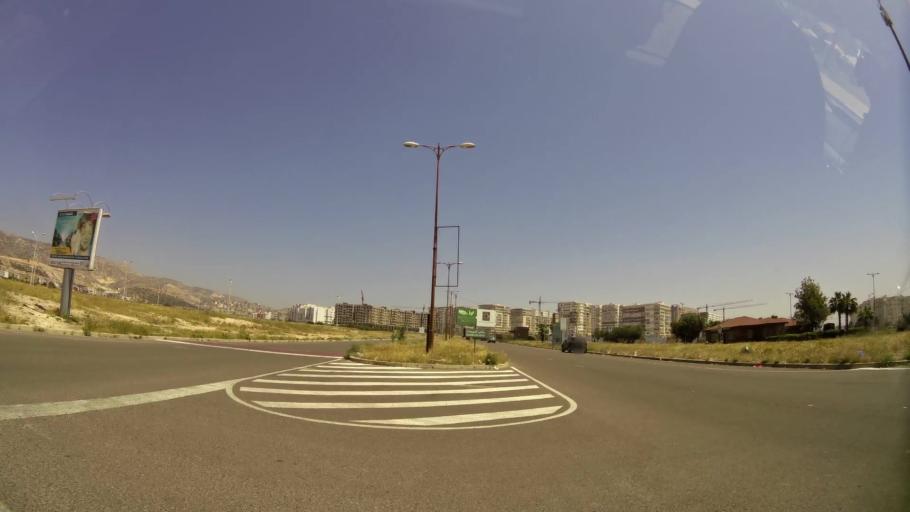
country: MA
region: Oued ed Dahab-Lagouira
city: Dakhla
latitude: 30.4371
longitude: -9.5703
